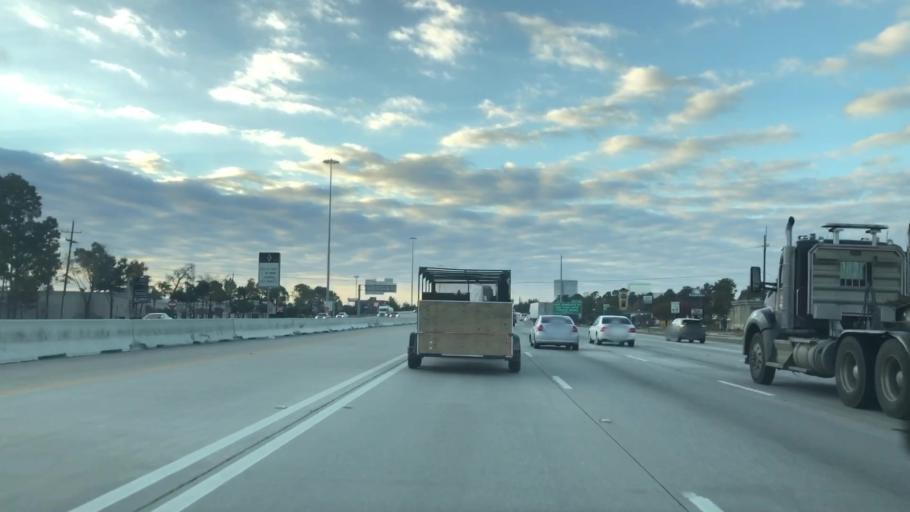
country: US
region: Texas
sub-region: Montgomery County
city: Shenandoah
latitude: 30.1842
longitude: -95.4525
